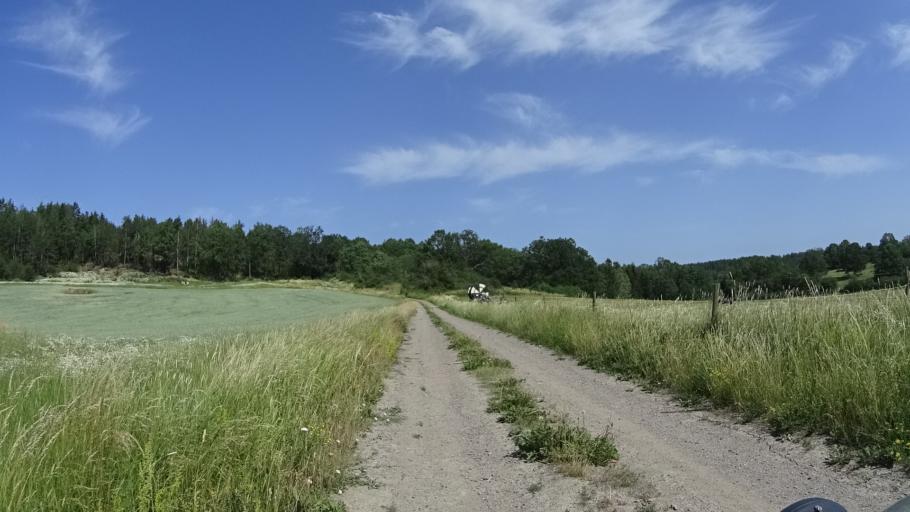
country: SE
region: Kalmar
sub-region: Vasterviks Kommun
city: Gamleby
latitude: 57.9177
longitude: 16.4063
